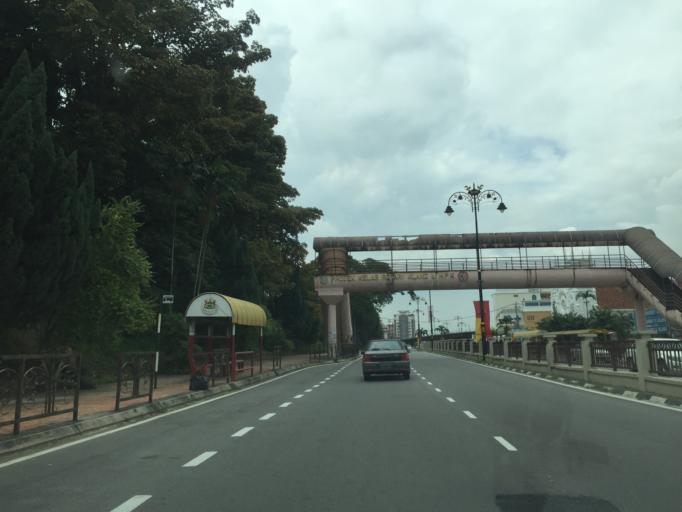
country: MY
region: Selangor
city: Klang
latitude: 3.0377
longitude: 101.4456
